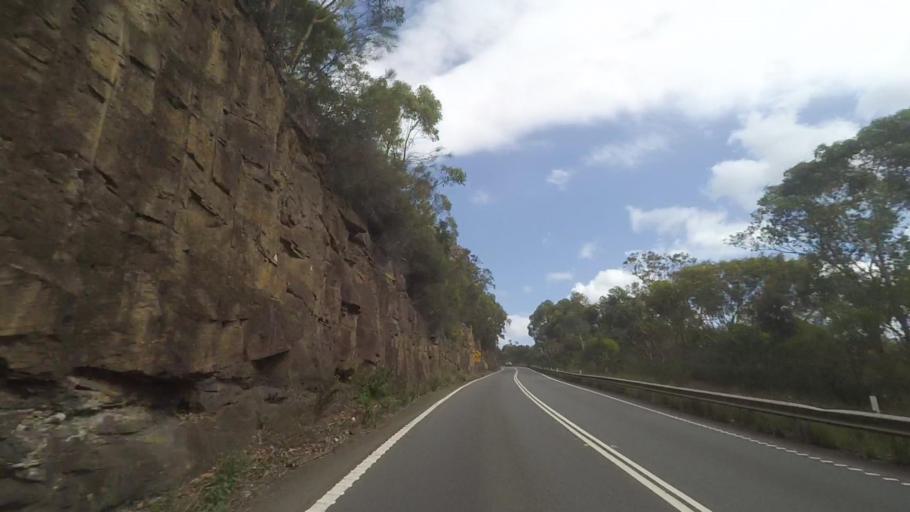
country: AU
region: New South Wales
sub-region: Sutherland Shire
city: Engadine
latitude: -34.0700
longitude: 150.9982
